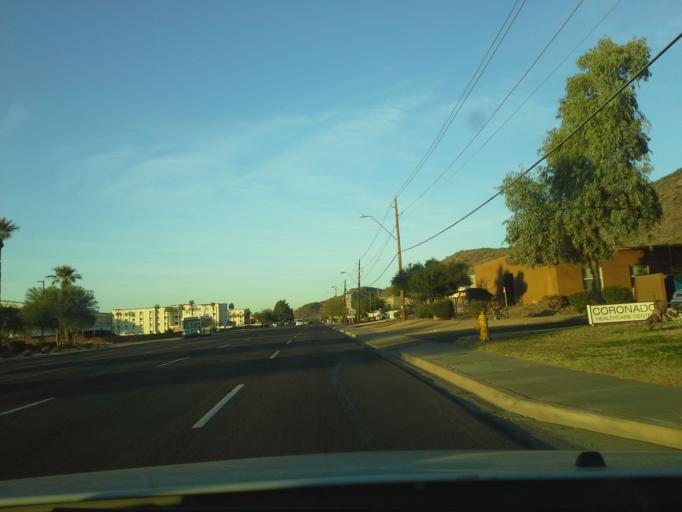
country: US
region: Arizona
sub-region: Maricopa County
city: Glendale
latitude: 33.5899
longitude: -112.0996
